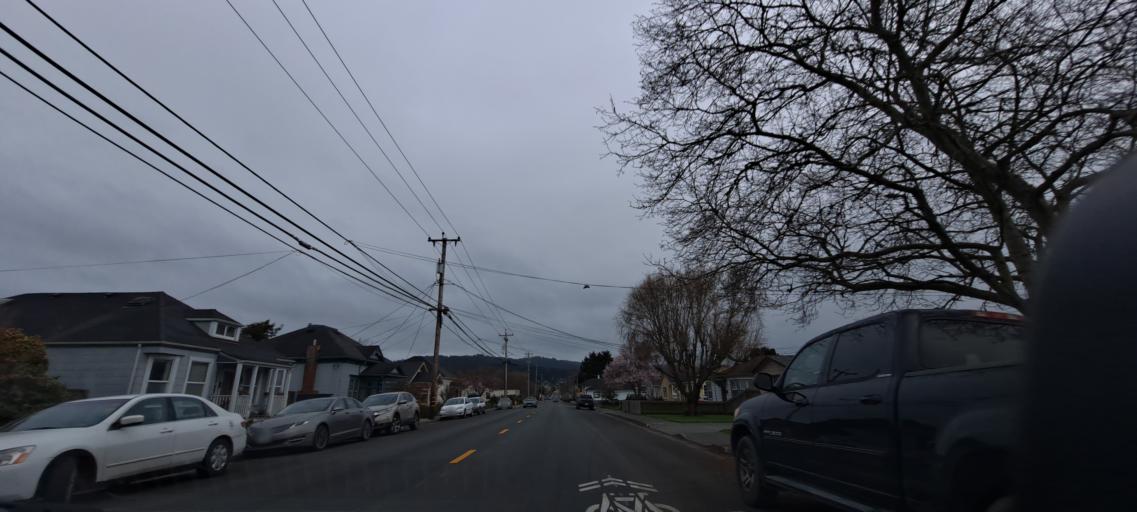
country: US
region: California
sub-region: Humboldt County
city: Arcata
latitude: 40.8724
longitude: -124.0946
